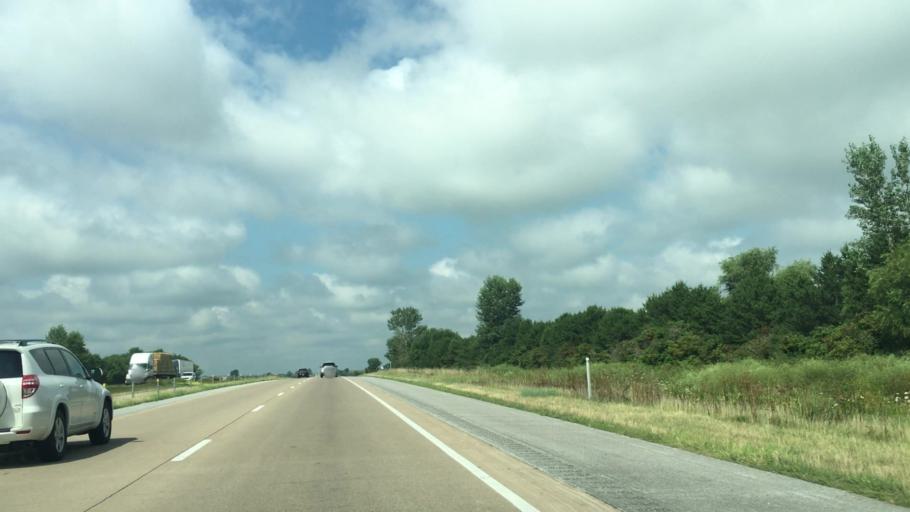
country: US
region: Iowa
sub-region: Cedar County
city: Durant
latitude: 41.6341
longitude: -90.9627
